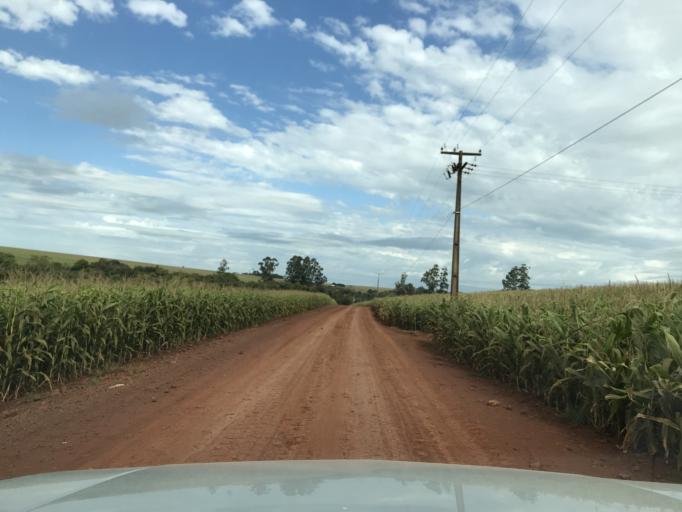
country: BR
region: Parana
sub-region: Palotina
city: Palotina
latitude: -24.3188
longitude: -53.8067
